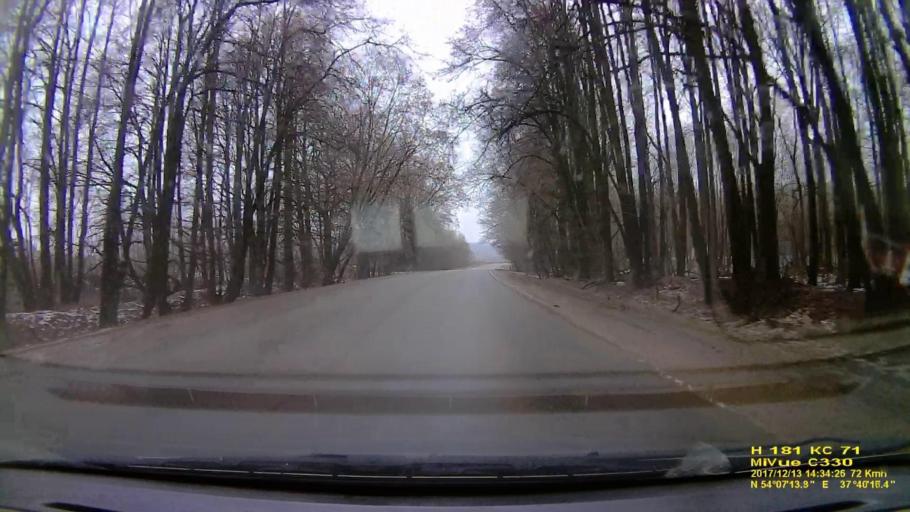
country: RU
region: Tula
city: Skuratovskiy
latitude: 54.1205
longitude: 37.6712
